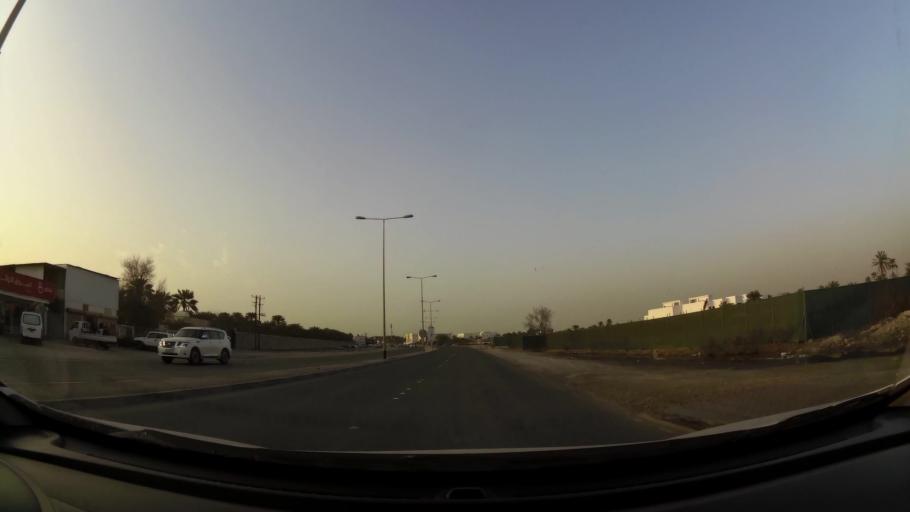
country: BH
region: Central Governorate
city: Madinat Hamad
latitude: 26.1866
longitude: 50.4660
